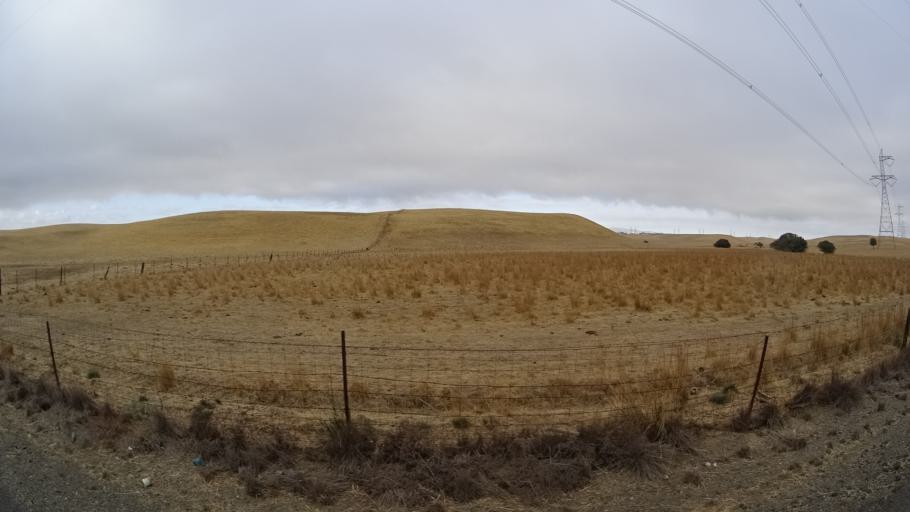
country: US
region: California
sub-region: Yolo County
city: Dunnigan
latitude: 38.8467
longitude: -122.0436
